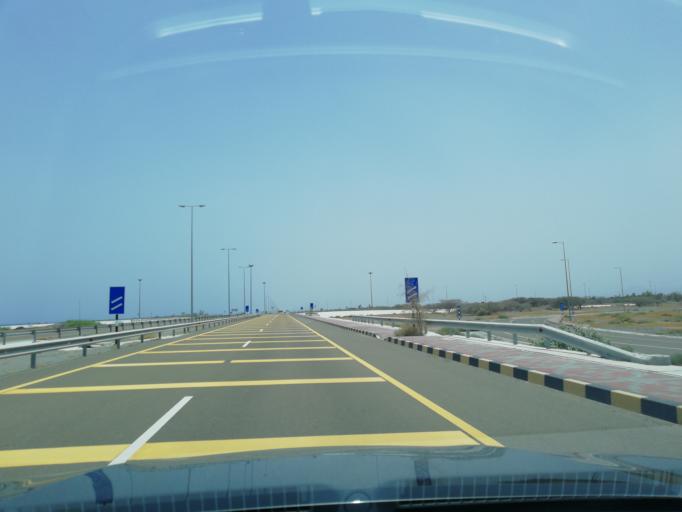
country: OM
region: Al Batinah
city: Shinas
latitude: 24.9199
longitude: 56.3873
